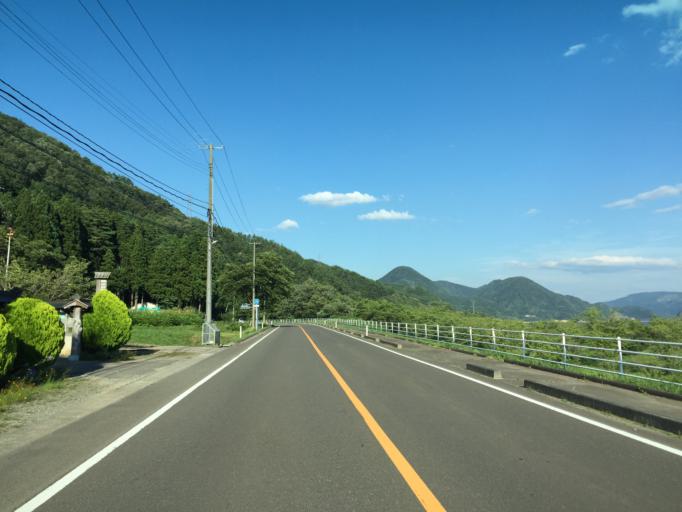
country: JP
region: Miyagi
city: Shiroishi
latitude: 37.9828
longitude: 140.4719
